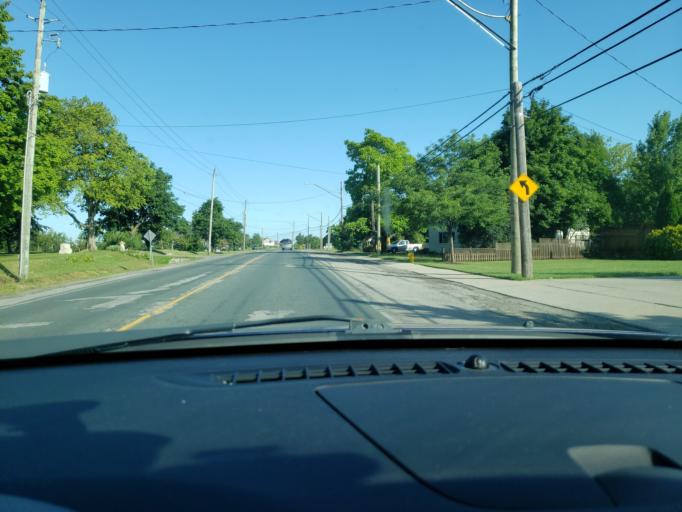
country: CA
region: Ontario
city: Hamilton
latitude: 43.1993
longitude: -79.6077
